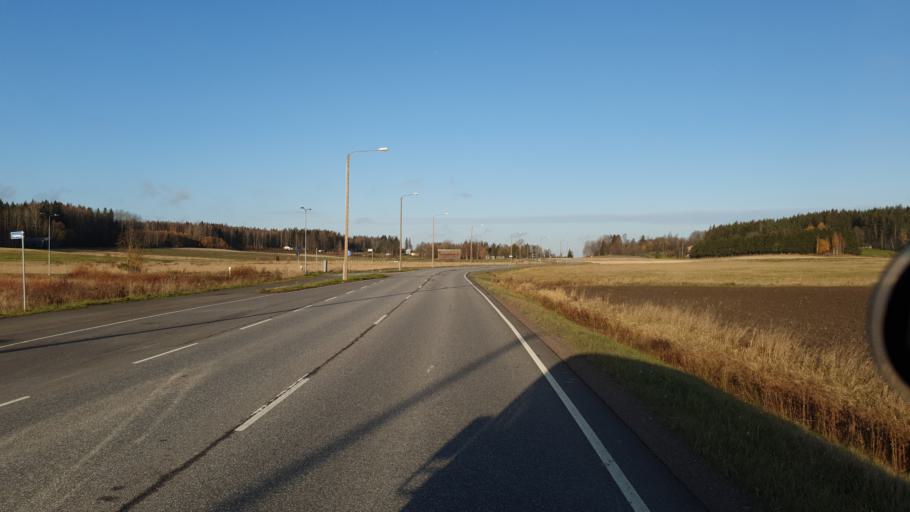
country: FI
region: Uusimaa
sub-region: Helsinki
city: Siuntio
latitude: 60.1471
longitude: 24.2183
